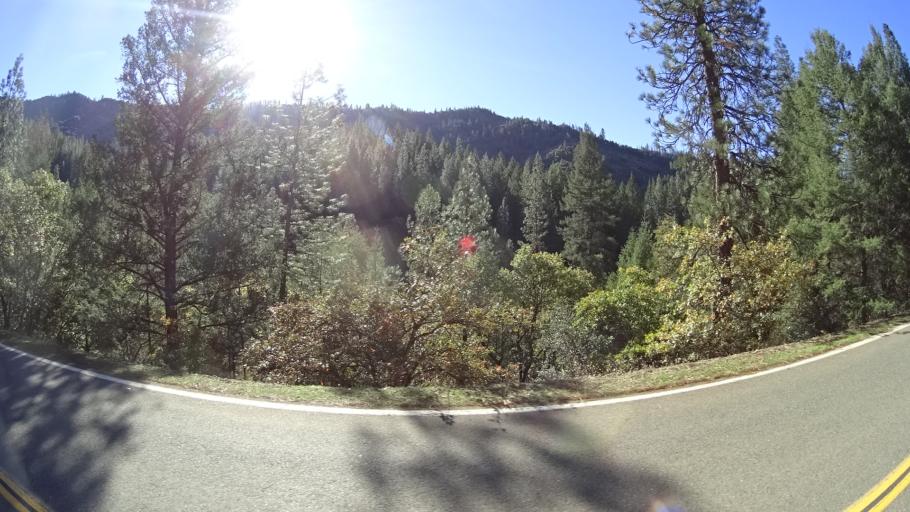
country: US
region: California
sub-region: Trinity County
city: Weaverville
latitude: 41.1584
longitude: -123.1007
